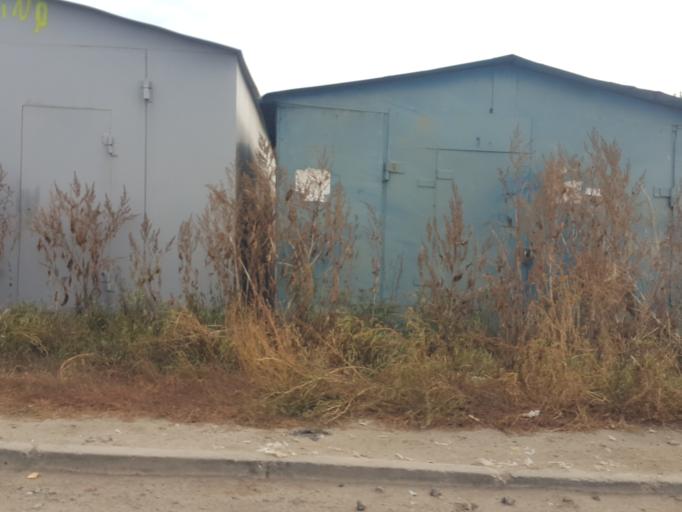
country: RU
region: Tambov
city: Pokrovo-Prigorodnoye
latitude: 52.6823
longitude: 41.4558
